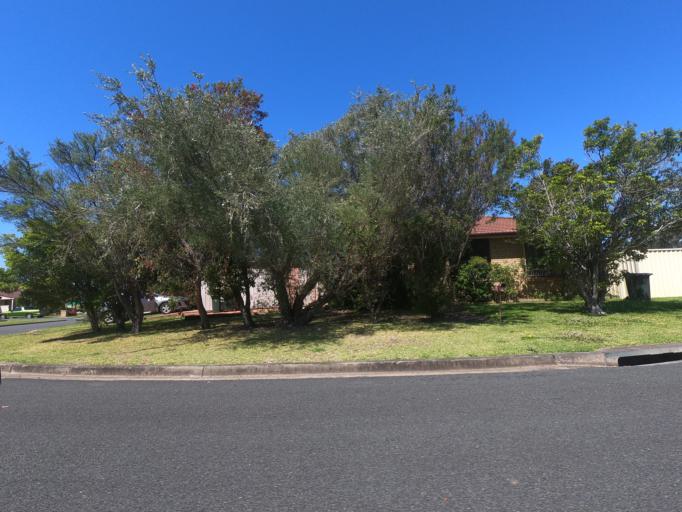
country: AU
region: New South Wales
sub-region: Wollongong
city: Dapto
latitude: -34.4831
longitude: 150.7810
